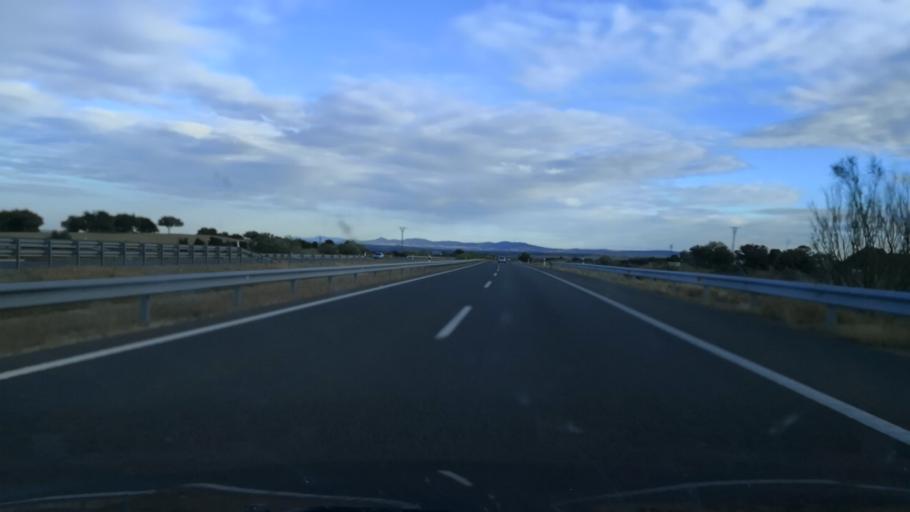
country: ES
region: Extremadura
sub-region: Provincia de Caceres
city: Santiago del Campo
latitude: 39.6423
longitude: -6.3948
